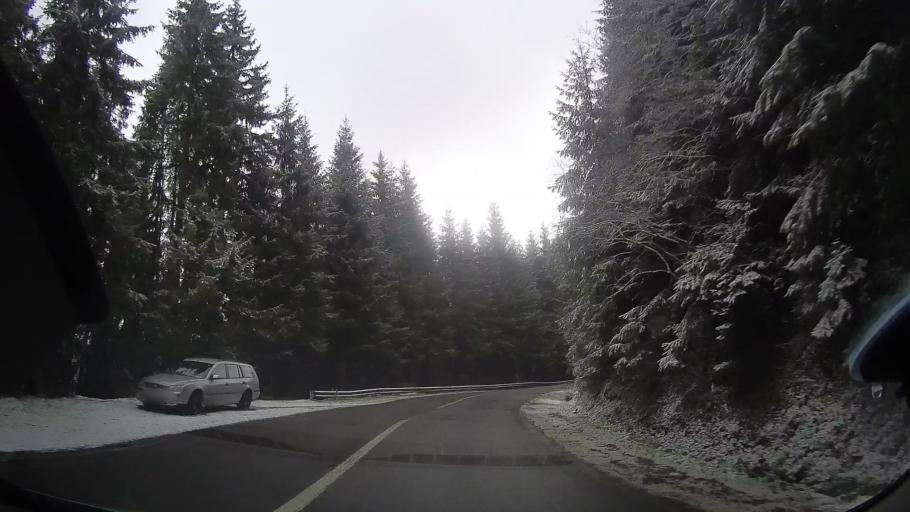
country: RO
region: Cluj
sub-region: Comuna Belis
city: Belis
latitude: 46.6603
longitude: 23.0563
